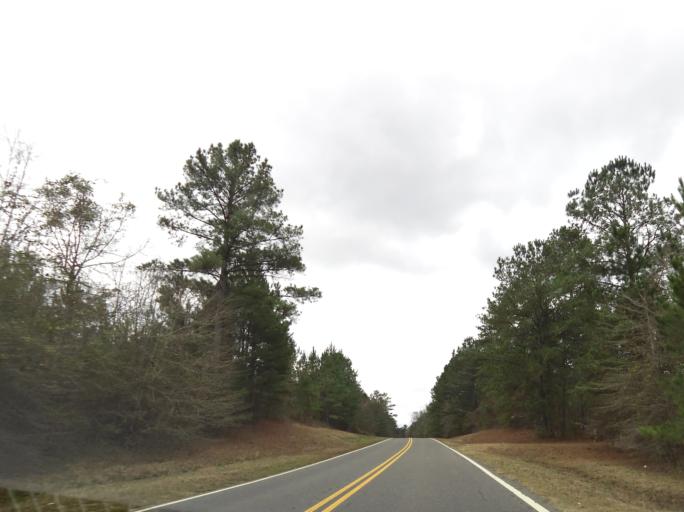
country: US
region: Georgia
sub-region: Bleckley County
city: Cochran
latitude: 32.5017
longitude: -83.3691
